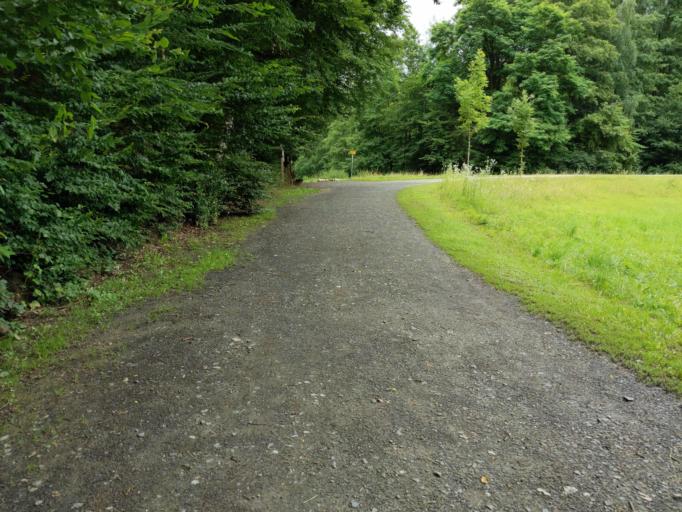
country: DE
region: Bavaria
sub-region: Regierungsbezirk Unterfranken
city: Geiselbach
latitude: 50.1373
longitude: 9.1694
